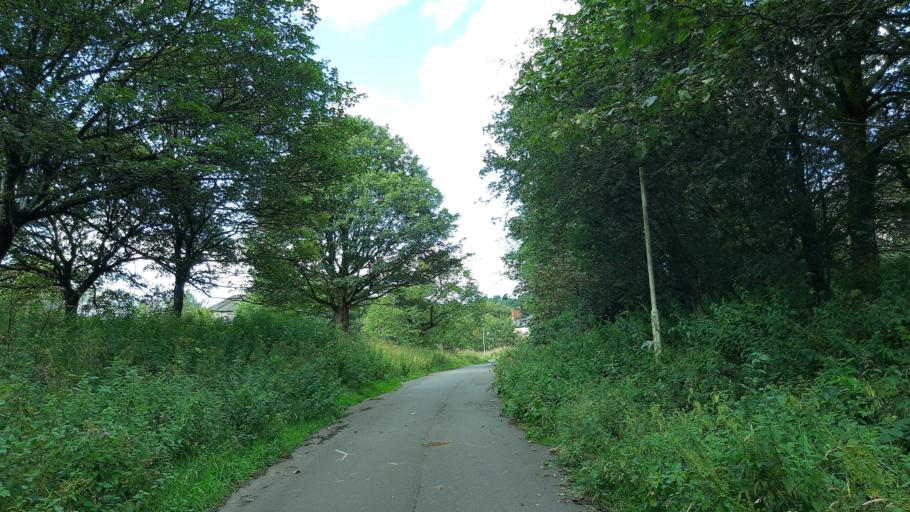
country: GB
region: Scotland
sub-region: West Lothian
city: Livingston
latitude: 55.9191
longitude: -3.5589
